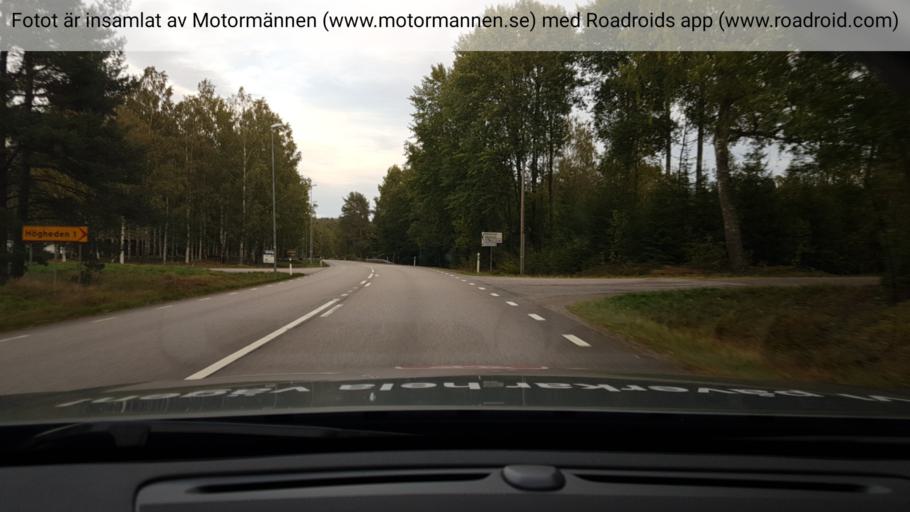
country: SE
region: Vaestra Goetaland
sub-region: Bengtsfors Kommun
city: Dals Langed
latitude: 59.0577
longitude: 12.4492
